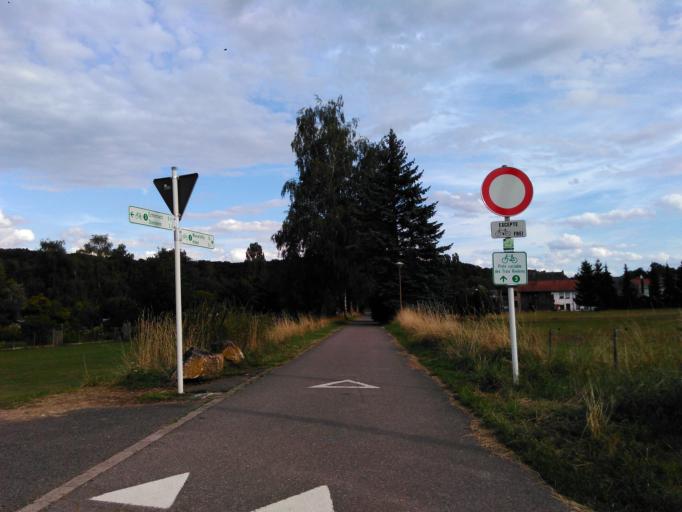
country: LU
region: Grevenmacher
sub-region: Canton d'Echternach
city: Rosport
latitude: 49.8072
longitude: 6.5051
